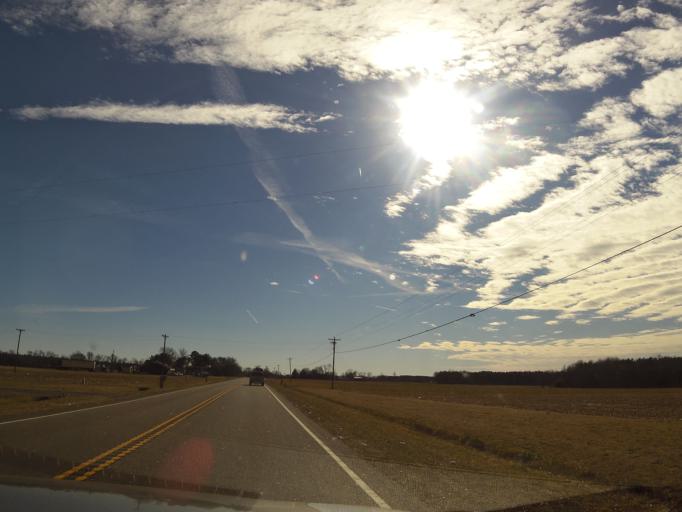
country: US
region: Virginia
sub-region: City of Franklin
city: Franklin
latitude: 36.7395
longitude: -76.8765
